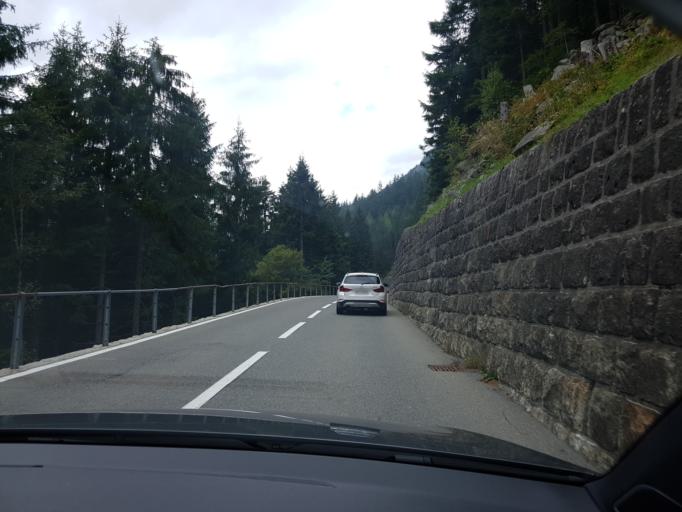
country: CH
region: Uri
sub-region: Uri
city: Andermatt
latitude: 46.7153
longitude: 8.5824
